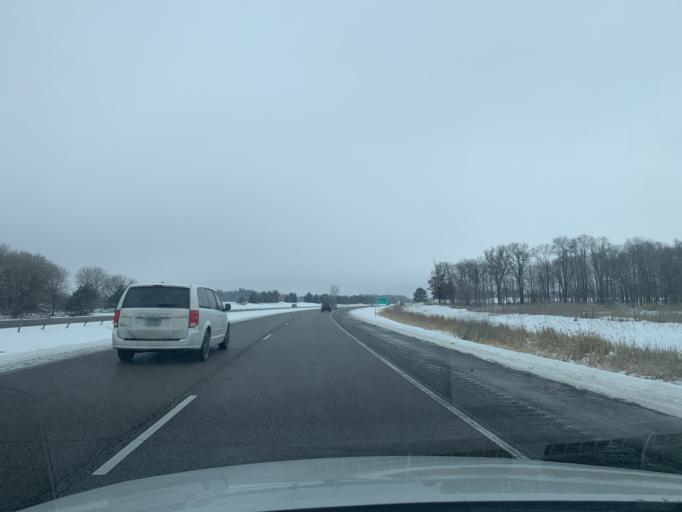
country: US
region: Minnesota
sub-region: Chisago County
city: Branch
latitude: 45.4619
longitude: -92.9952
